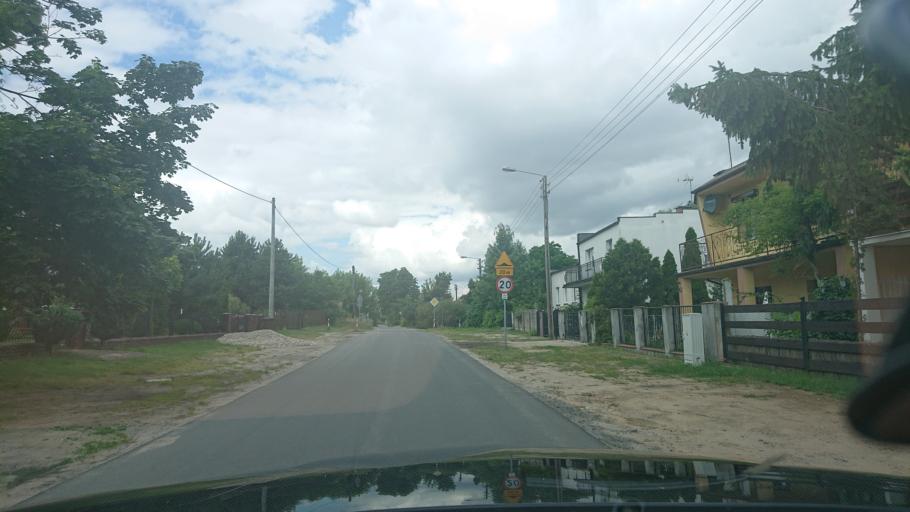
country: PL
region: Greater Poland Voivodeship
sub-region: Powiat gnieznienski
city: Gniezno
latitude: 52.5142
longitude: 17.6187
